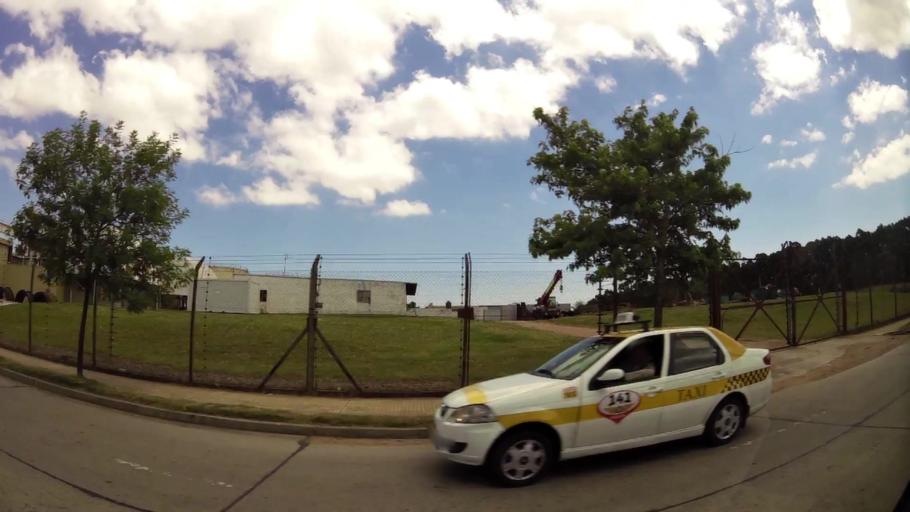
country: UY
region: Canelones
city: La Paz
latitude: -34.8256
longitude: -56.2369
